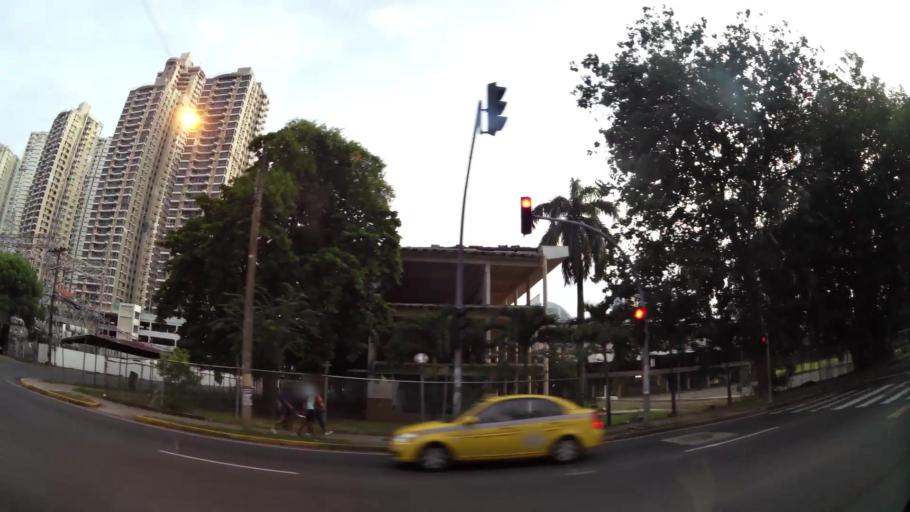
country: PA
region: Panama
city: Panama
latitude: 8.9877
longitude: -79.5044
